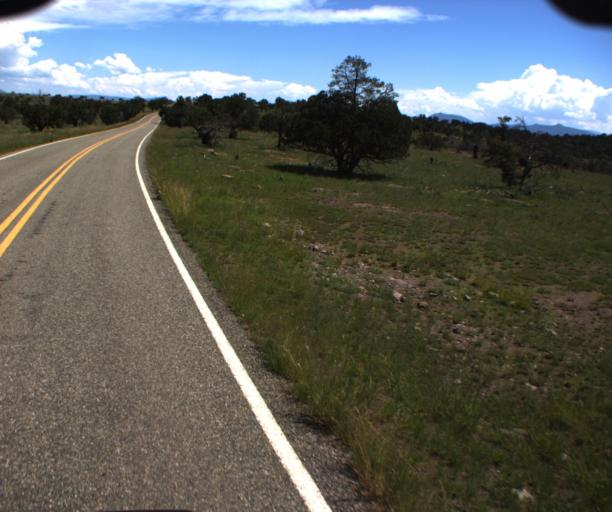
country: US
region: Arizona
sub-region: Greenlee County
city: Morenci
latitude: 33.2988
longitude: -109.3597
